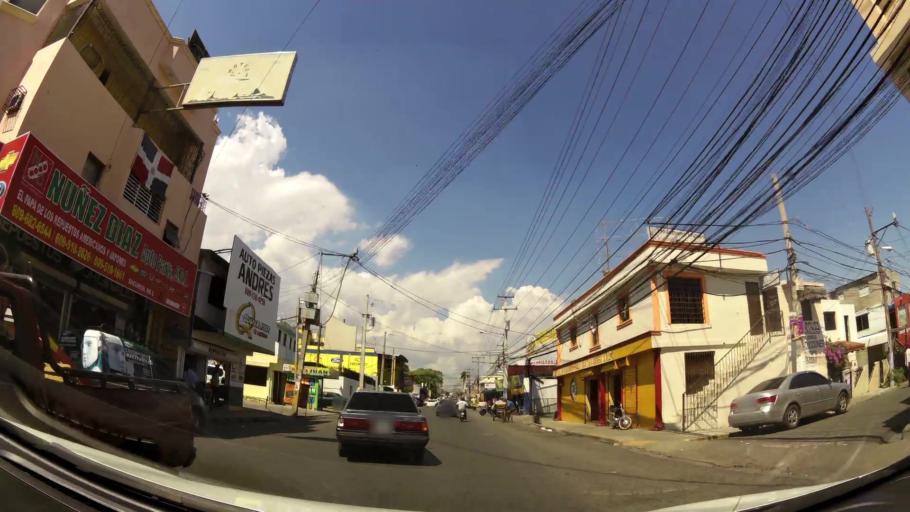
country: DO
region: Nacional
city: Bella Vista
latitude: 18.4624
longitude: -69.9758
